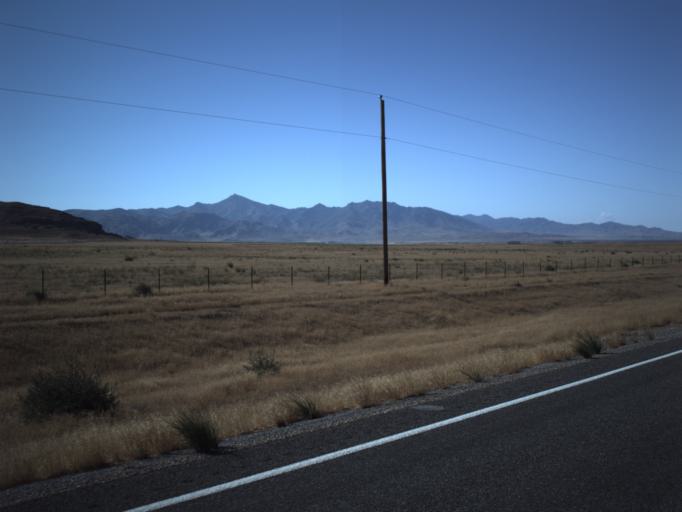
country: US
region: Utah
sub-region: Millard County
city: Delta
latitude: 39.6100
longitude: -112.3202
